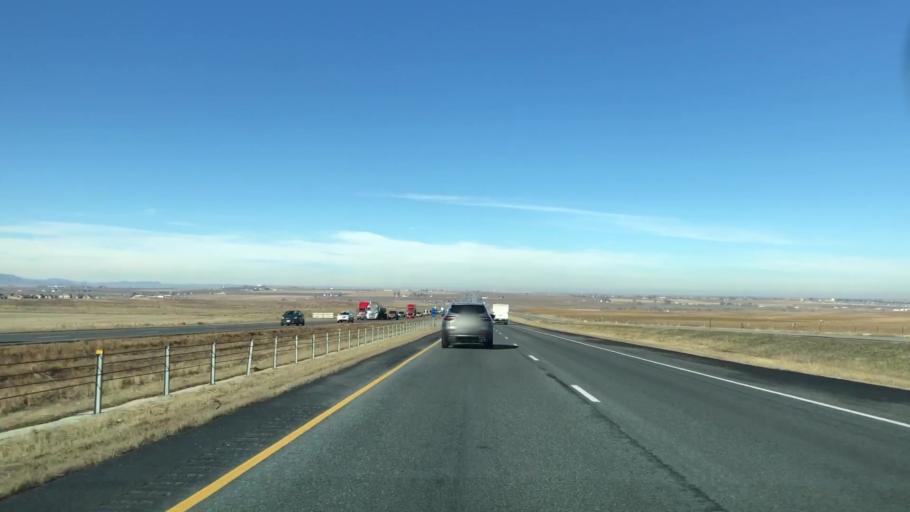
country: US
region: Colorado
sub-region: Weld County
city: Mead
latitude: 40.2751
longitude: -104.9801
